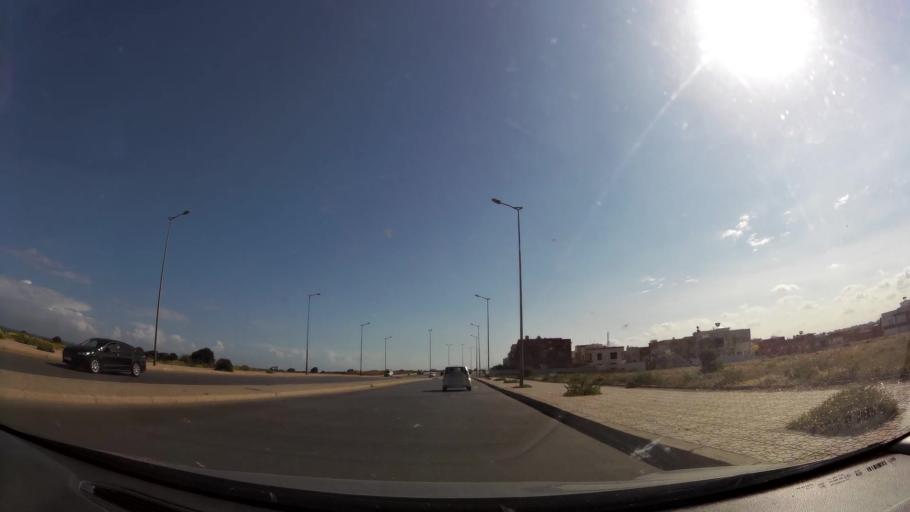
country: MA
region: Rabat-Sale-Zemmour-Zaer
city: Sale
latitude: 34.0720
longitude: -6.8018
